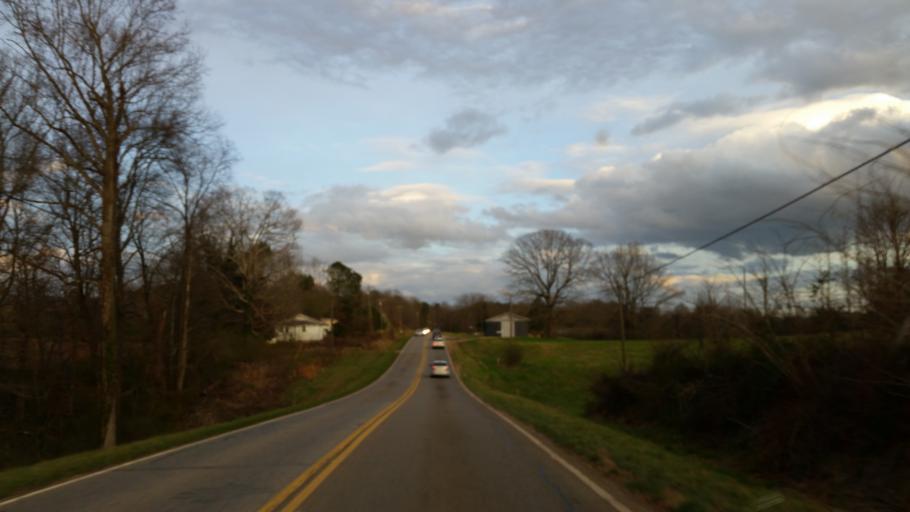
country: US
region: Georgia
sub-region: Pickens County
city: Jasper
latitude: 34.4682
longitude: -84.4918
